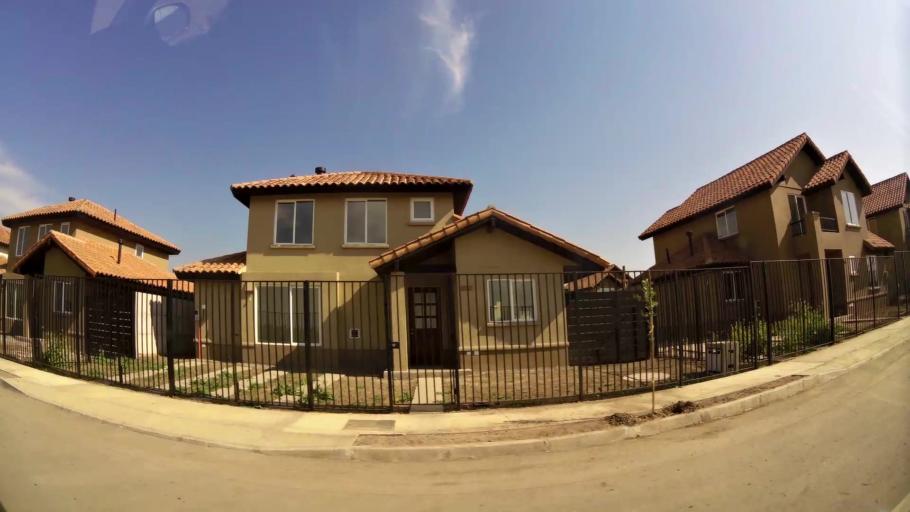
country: CL
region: Santiago Metropolitan
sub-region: Provincia de Talagante
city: Penaflor
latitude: -33.5664
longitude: -70.8294
